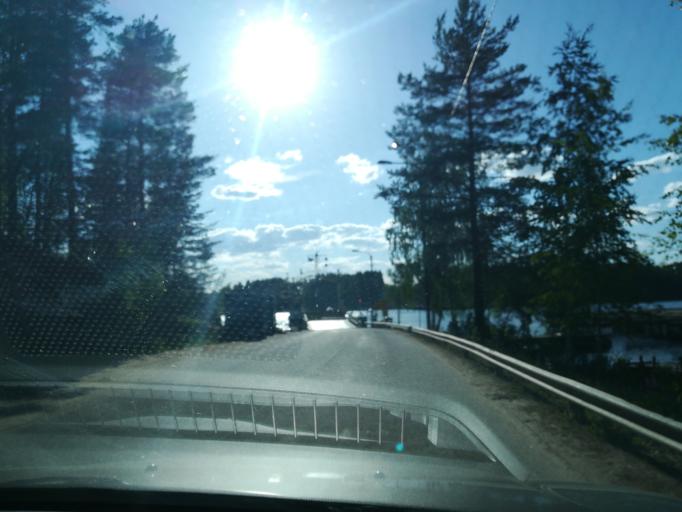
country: FI
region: Southern Savonia
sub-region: Savonlinna
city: Sulkava
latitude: 61.7379
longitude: 28.5041
